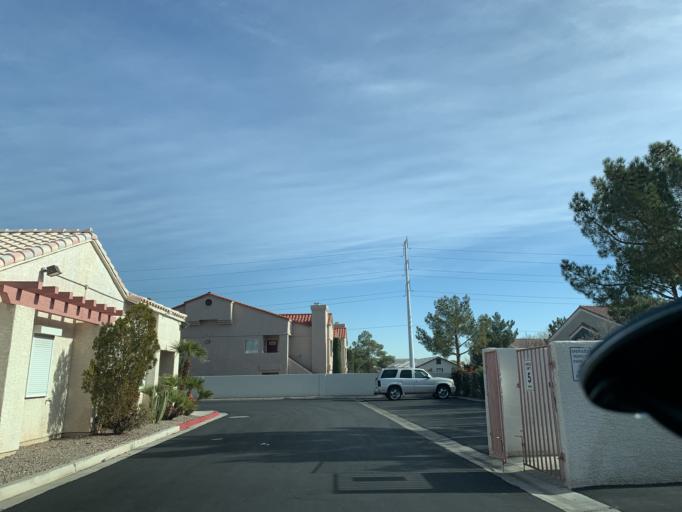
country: US
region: Nevada
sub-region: Clark County
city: Spring Valley
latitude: 36.0952
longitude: -115.2138
